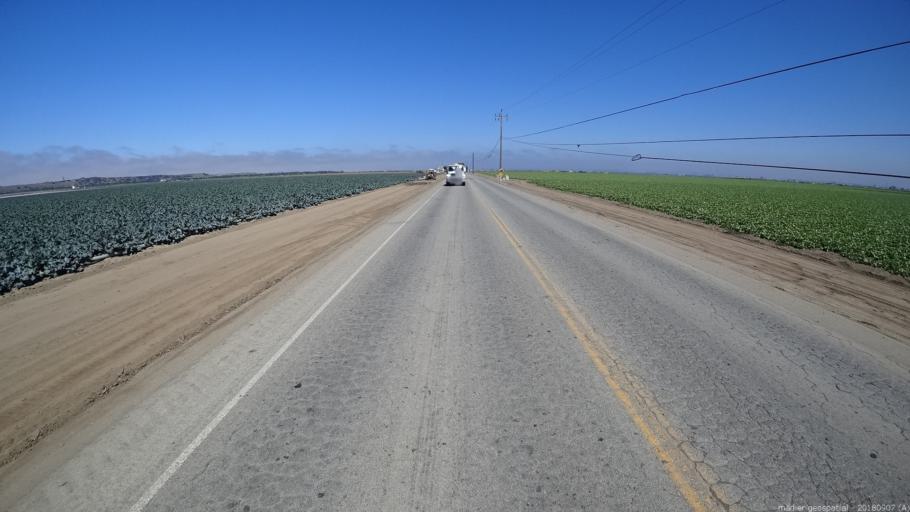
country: US
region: California
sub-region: Monterey County
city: Boronda
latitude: 36.6798
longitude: -121.7351
